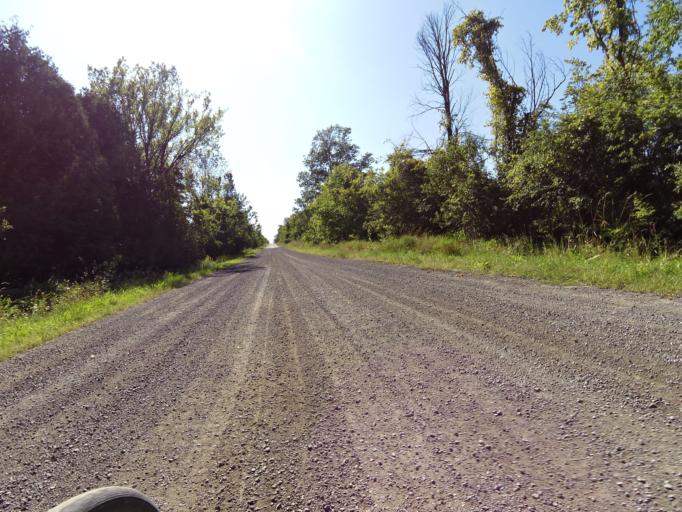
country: CA
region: Ontario
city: Bells Corners
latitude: 45.4250
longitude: -75.9410
